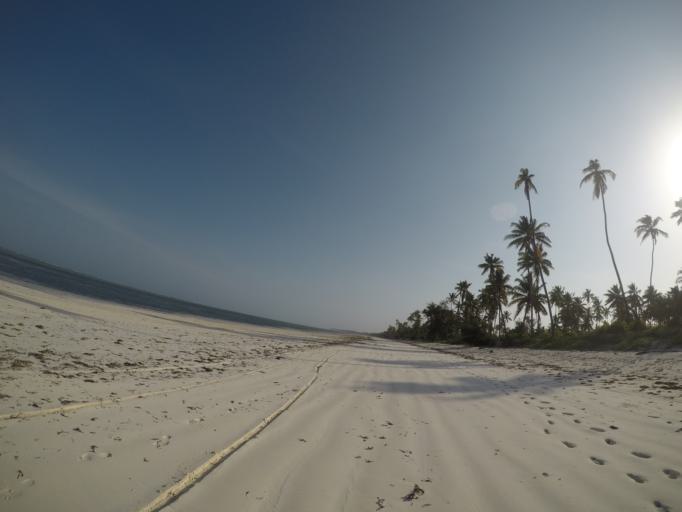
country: TZ
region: Zanzibar Central/South
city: Nganane
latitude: -6.2072
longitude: 39.5347
